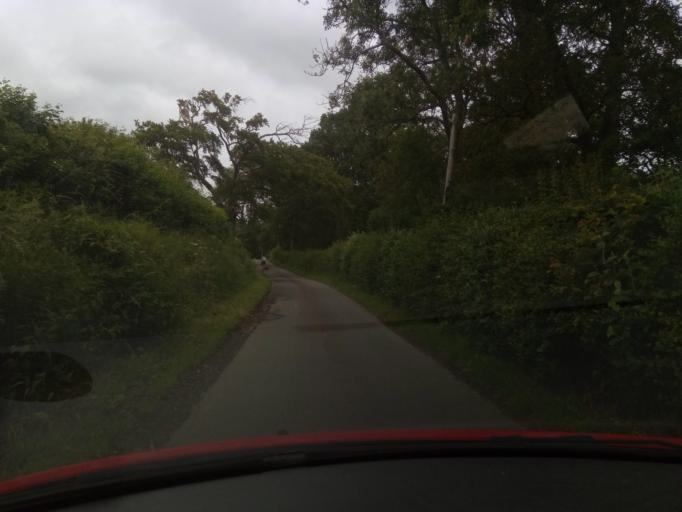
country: GB
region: Scotland
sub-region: The Scottish Borders
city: Hawick
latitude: 55.4561
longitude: -2.7304
